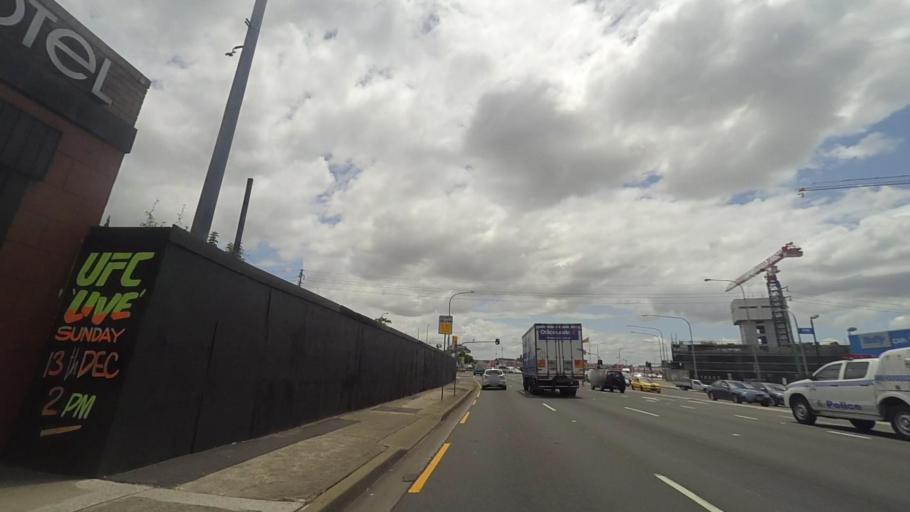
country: AU
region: New South Wales
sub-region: Fairfield
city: Liverpool
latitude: -33.9295
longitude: 150.9177
